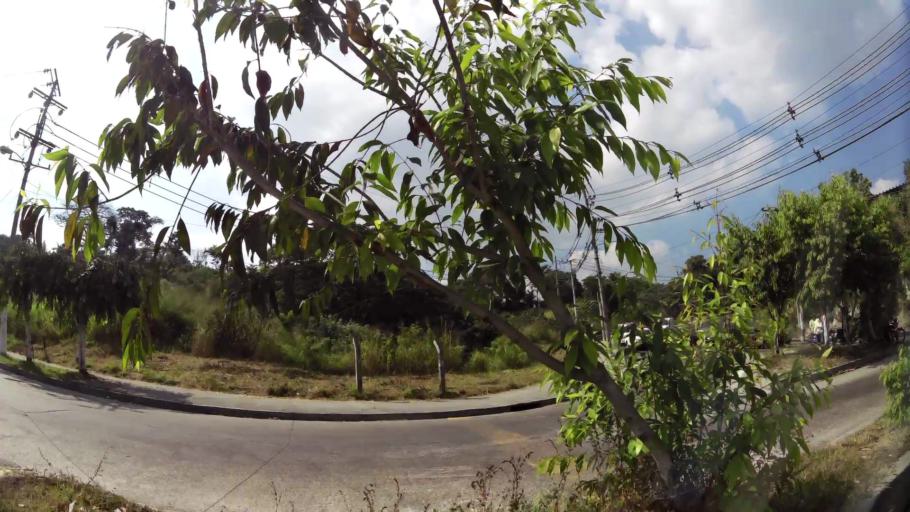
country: SV
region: San Salvador
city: Delgado
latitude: 13.7068
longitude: -89.1706
